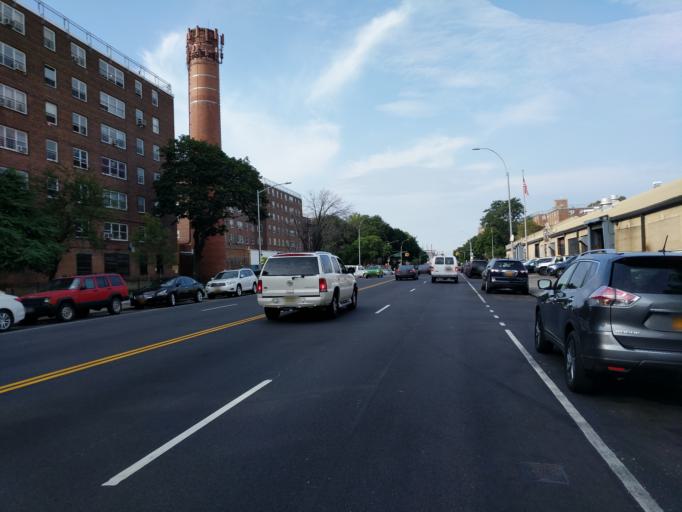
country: US
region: New York
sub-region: Queens County
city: Long Island City
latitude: 40.7625
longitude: -73.9345
